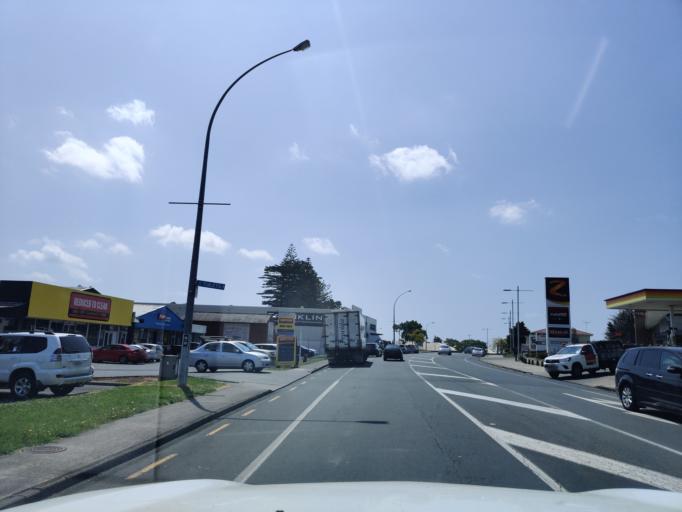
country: NZ
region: Auckland
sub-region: Auckland
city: Pukekohe East
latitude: -37.2004
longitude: 174.9084
